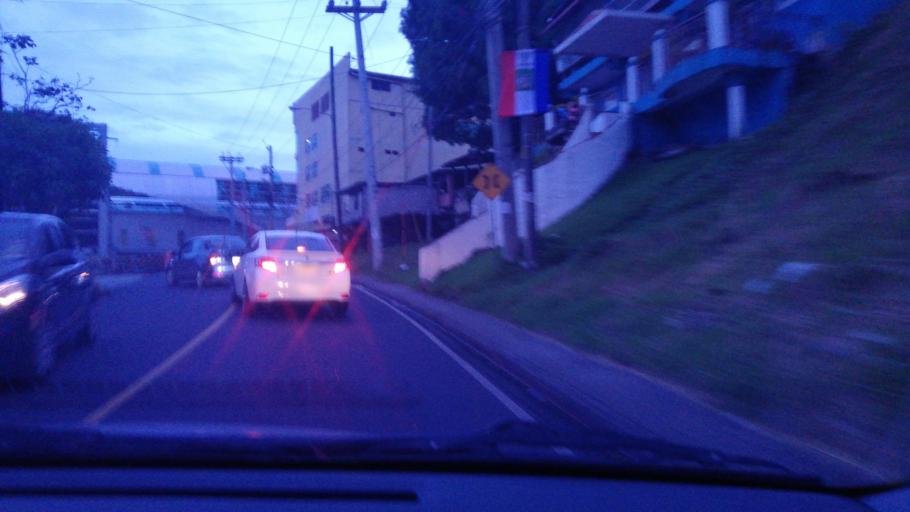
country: PA
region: Panama
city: San Miguelito
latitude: 9.0315
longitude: -79.4919
